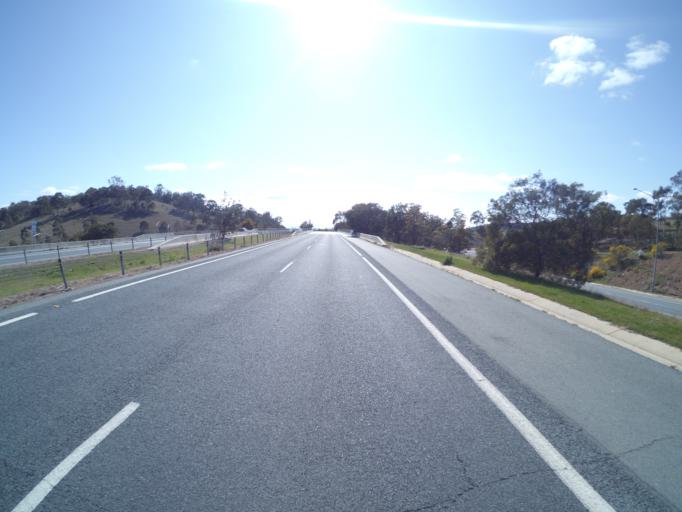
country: AU
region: Australian Capital Territory
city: Kaleen
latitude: -35.2144
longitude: 149.1866
